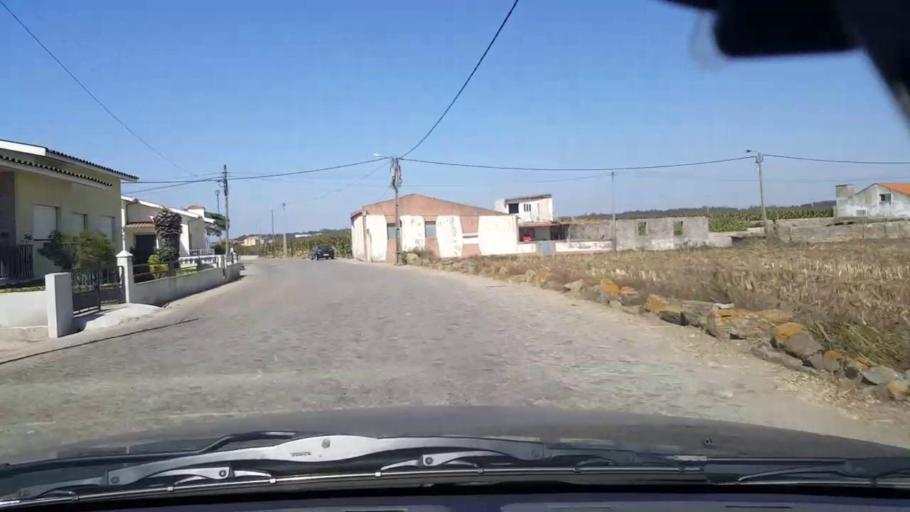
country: PT
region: Porto
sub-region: Matosinhos
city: Lavra
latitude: 41.2842
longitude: -8.7241
